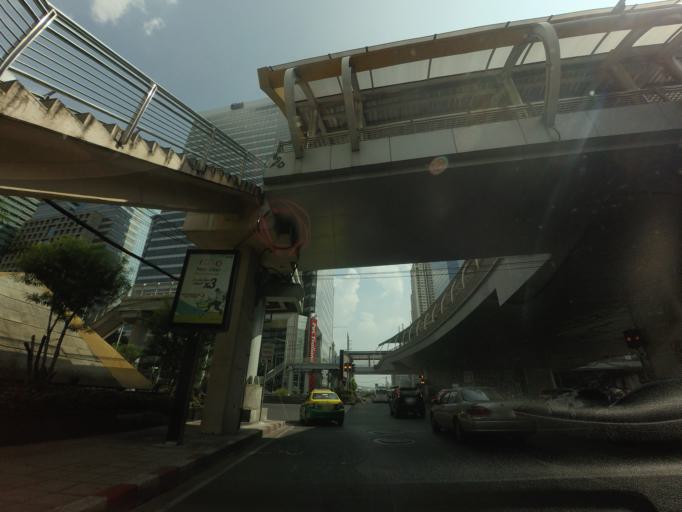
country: TH
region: Bangkok
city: Bang Rak
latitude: 13.7224
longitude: 100.5302
